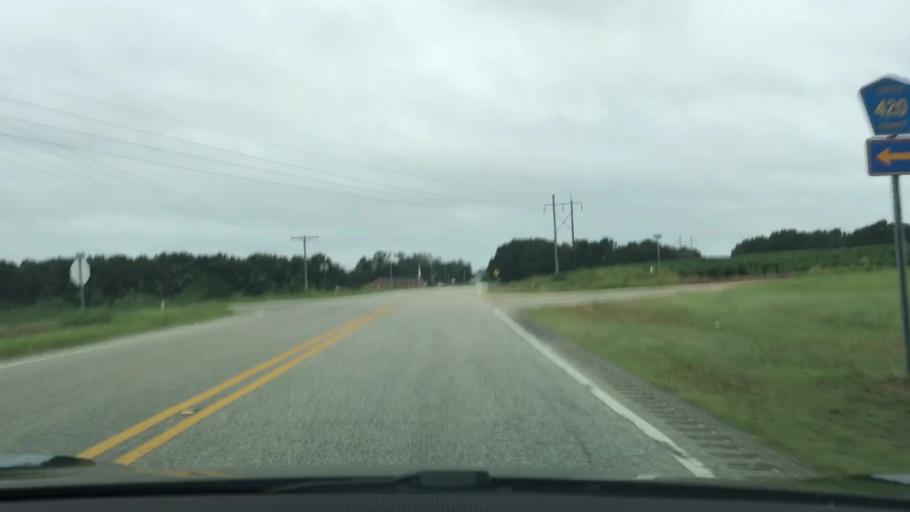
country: US
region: Alabama
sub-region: Coffee County
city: Elba
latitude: 31.3386
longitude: -86.1314
